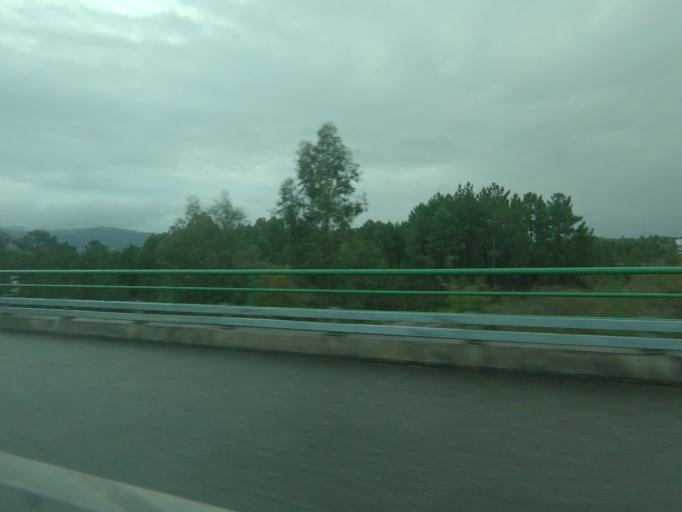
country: PT
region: Viana do Castelo
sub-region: Valenca
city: Valenza
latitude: 41.9727
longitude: -8.6627
